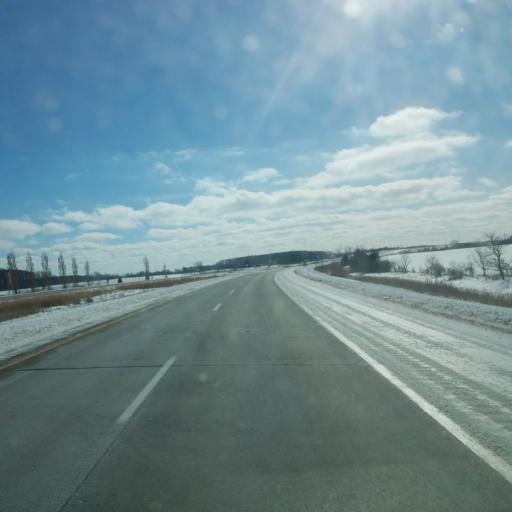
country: US
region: Michigan
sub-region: Clinton County
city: Saint Johns
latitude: 43.0153
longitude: -84.5210
